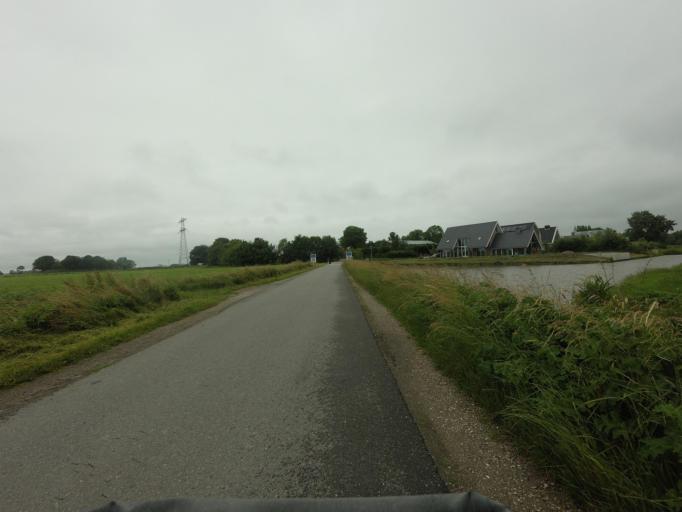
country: NL
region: North Holland
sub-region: Gemeente Schagen
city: Schagen
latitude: 52.7712
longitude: 4.8312
